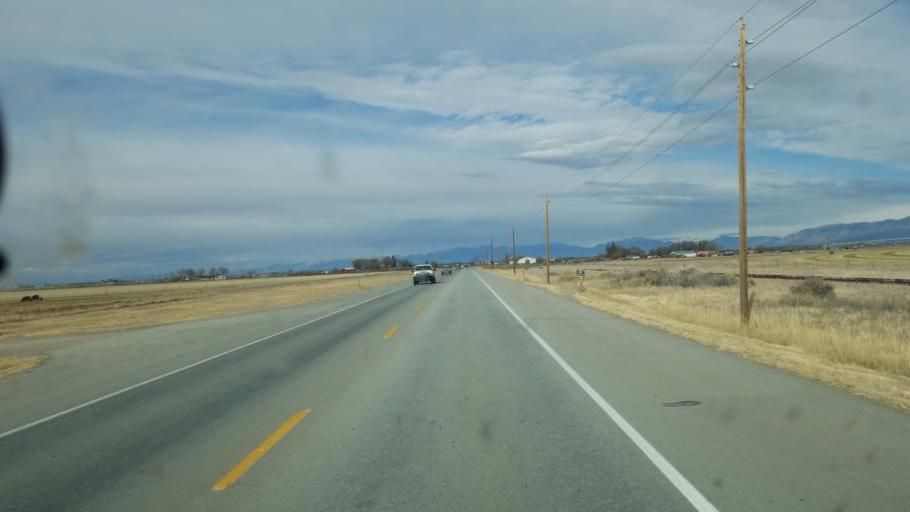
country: US
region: Colorado
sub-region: Alamosa County
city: Alamosa
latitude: 37.4093
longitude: -105.9017
